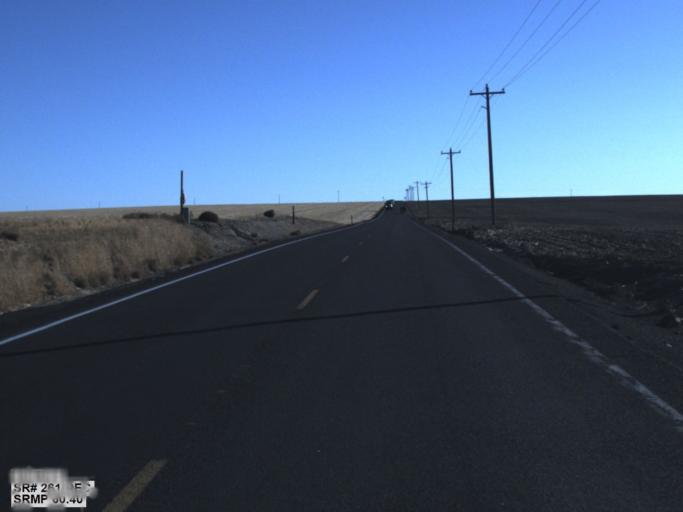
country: US
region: Washington
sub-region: Adams County
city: Ritzville
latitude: 47.0819
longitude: -118.3654
